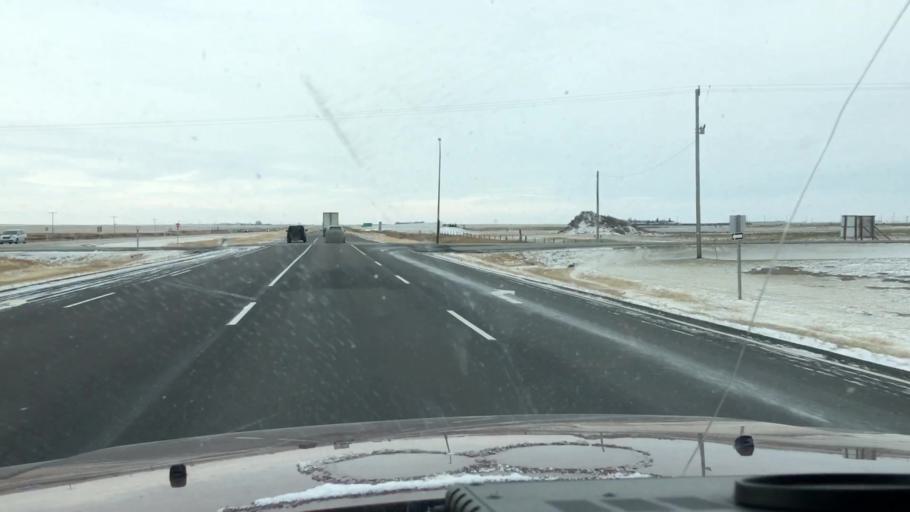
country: CA
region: Saskatchewan
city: Saskatoon
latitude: 51.8096
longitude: -106.4955
